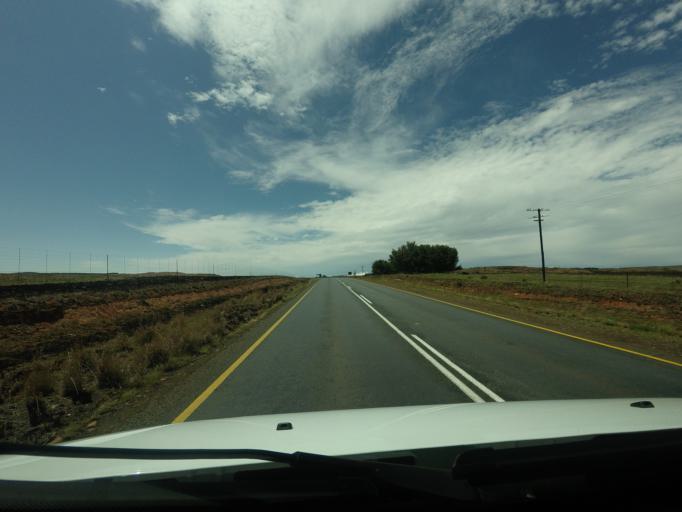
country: ZA
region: Mpumalanga
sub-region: Nkangala District Municipality
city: Belfast
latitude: -25.3983
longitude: 30.1251
